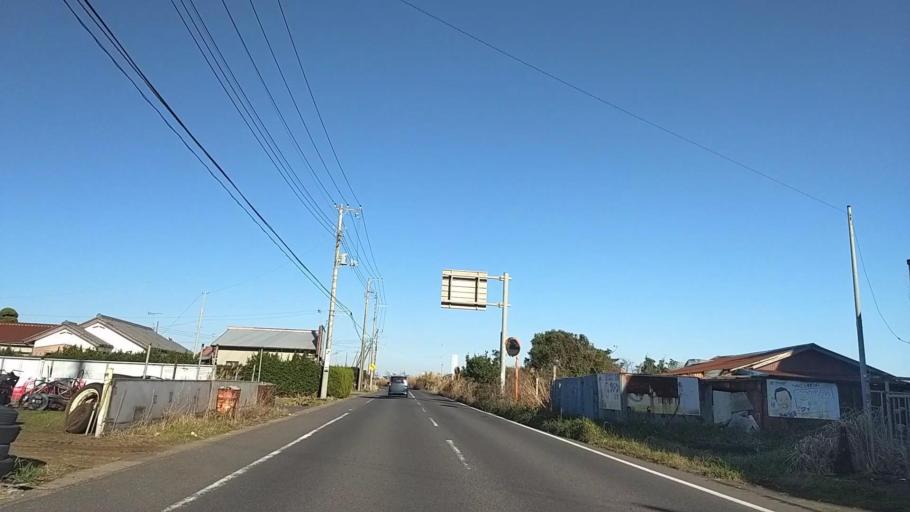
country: JP
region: Chiba
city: Asahi
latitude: 35.6708
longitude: 140.6170
